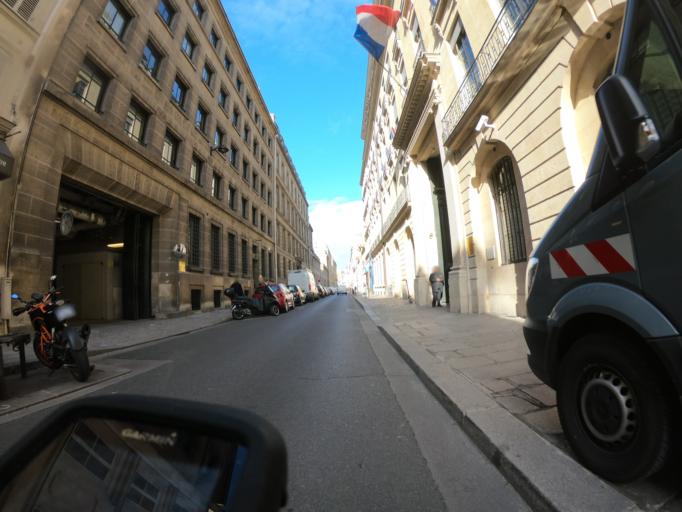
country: FR
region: Ile-de-France
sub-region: Paris
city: Paris
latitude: 48.8565
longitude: 2.3209
